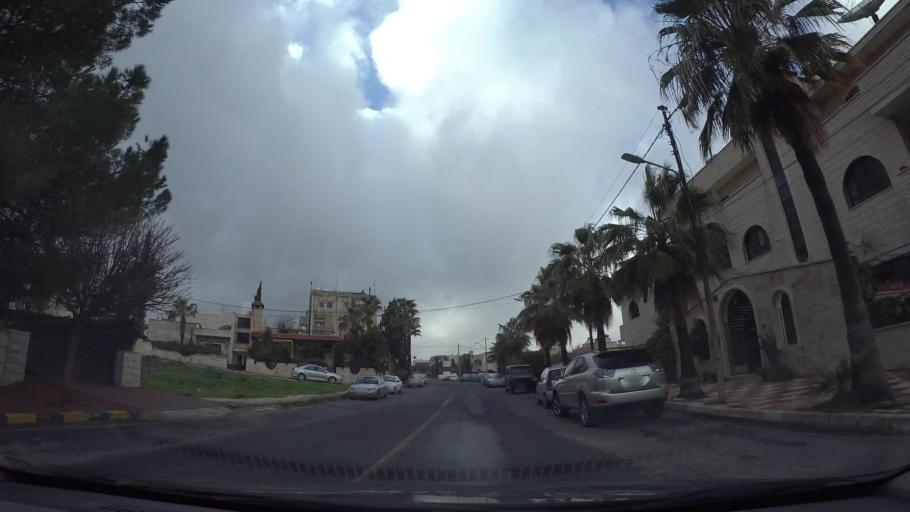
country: JO
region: Amman
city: Amman
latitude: 31.9479
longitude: 35.9003
